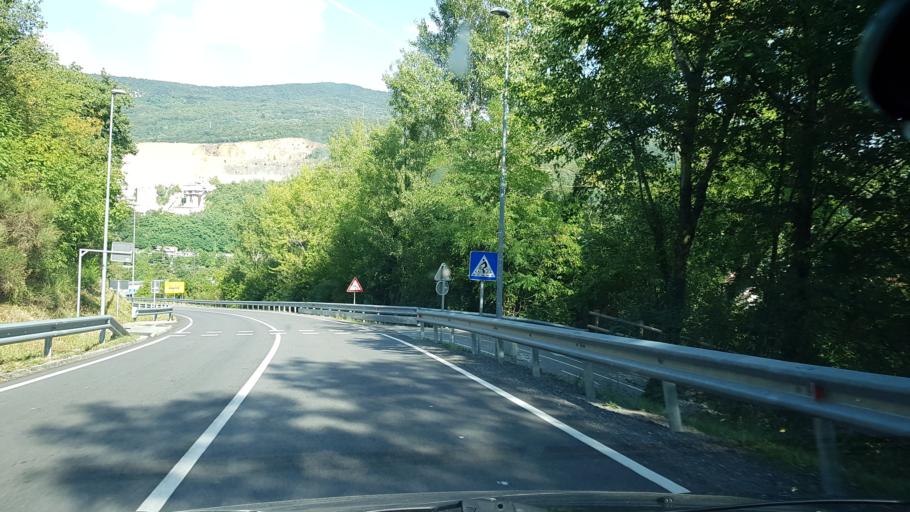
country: SI
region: Nova Gorica
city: Solkan
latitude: 45.9758
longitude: 13.6442
